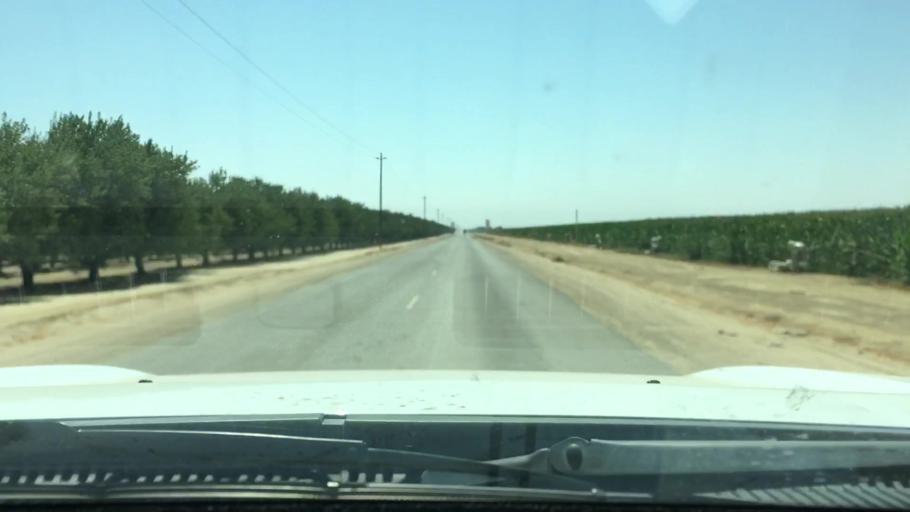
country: US
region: California
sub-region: Kern County
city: Wasco
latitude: 35.5758
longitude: -119.4028
